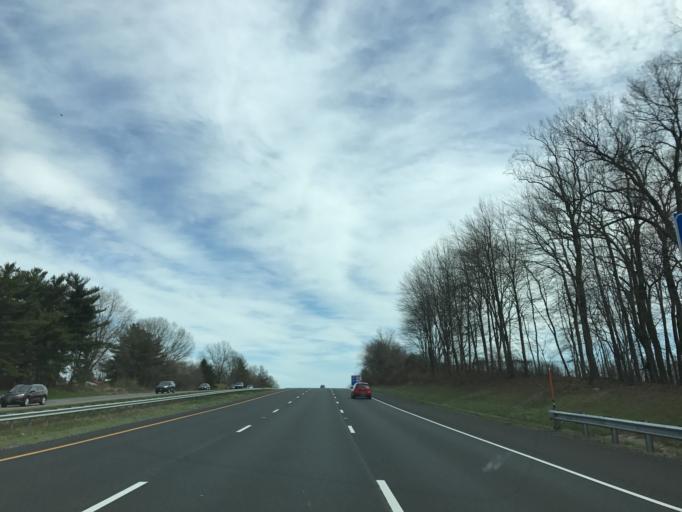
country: US
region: Maryland
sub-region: Frederick County
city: Spring Ridge
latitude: 39.3849
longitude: -77.2911
